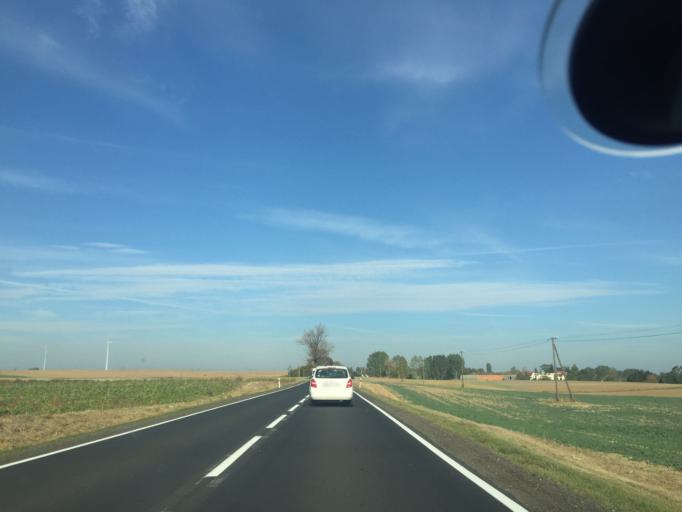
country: PL
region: Greater Poland Voivodeship
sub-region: Powiat gnieznienski
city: Trzemeszno
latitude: 52.5806
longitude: 17.8676
